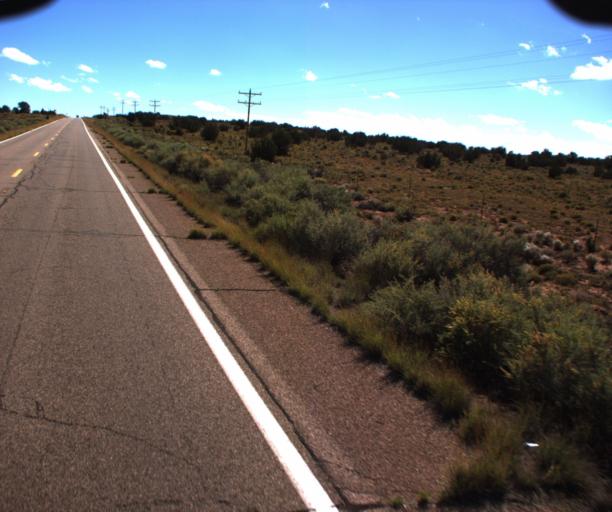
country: US
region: Arizona
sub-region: Apache County
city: Saint Johns
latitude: 34.5435
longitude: -109.6224
